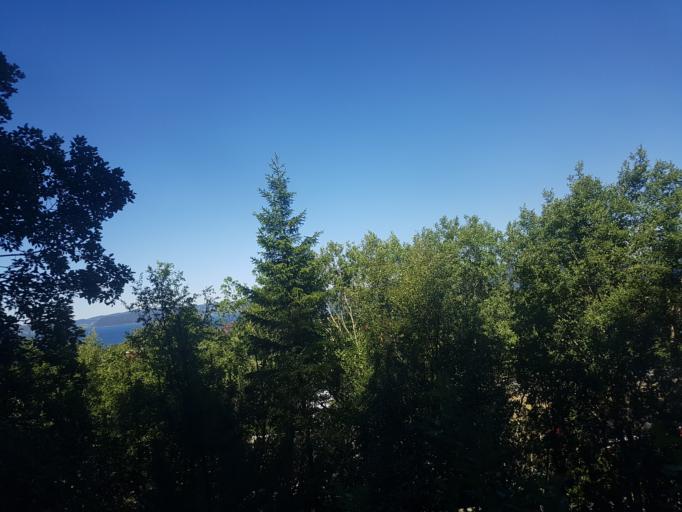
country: NO
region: Sor-Trondelag
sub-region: Skaun
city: Borsa
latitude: 63.4443
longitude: 10.1966
